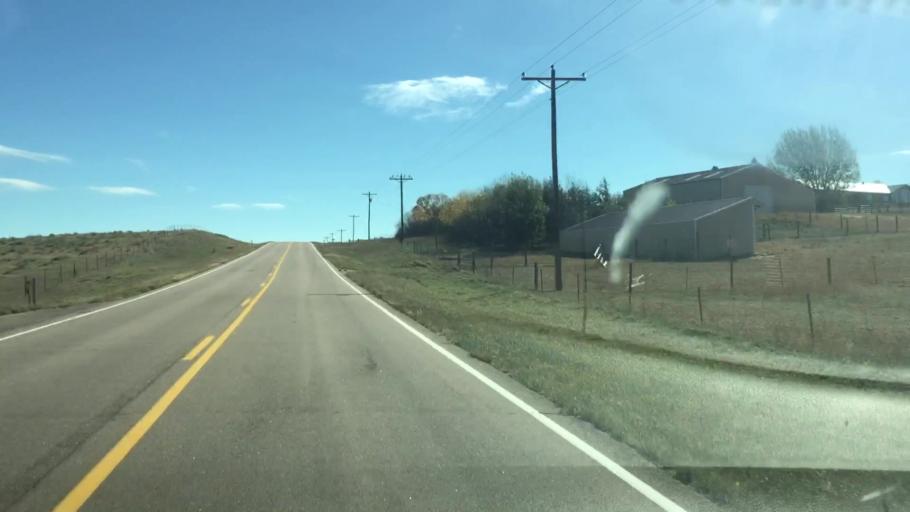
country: US
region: Colorado
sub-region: Elbert County
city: Kiowa
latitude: 39.2736
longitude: -104.1323
